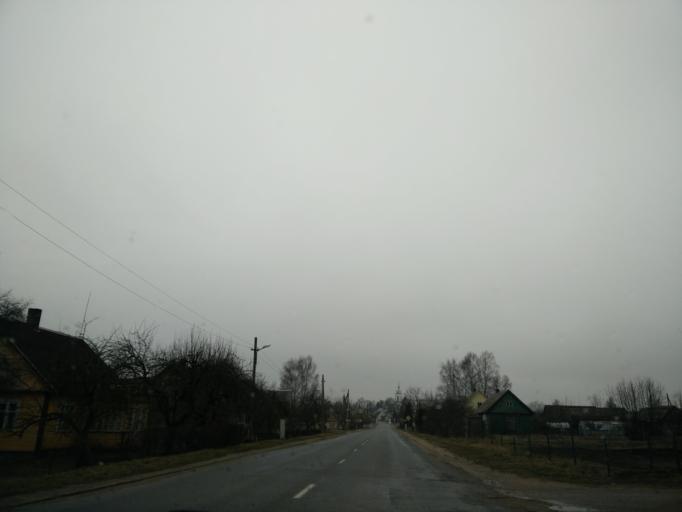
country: LT
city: Ariogala
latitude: 55.3586
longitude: 23.3724
